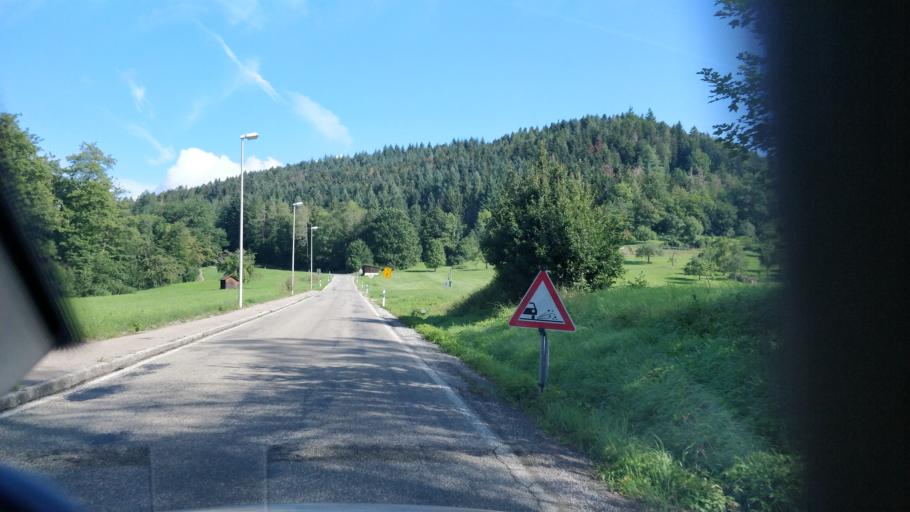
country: DE
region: Baden-Wuerttemberg
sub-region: Regierungsbezirk Stuttgart
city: Murrhardt
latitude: 48.9900
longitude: 9.5854
